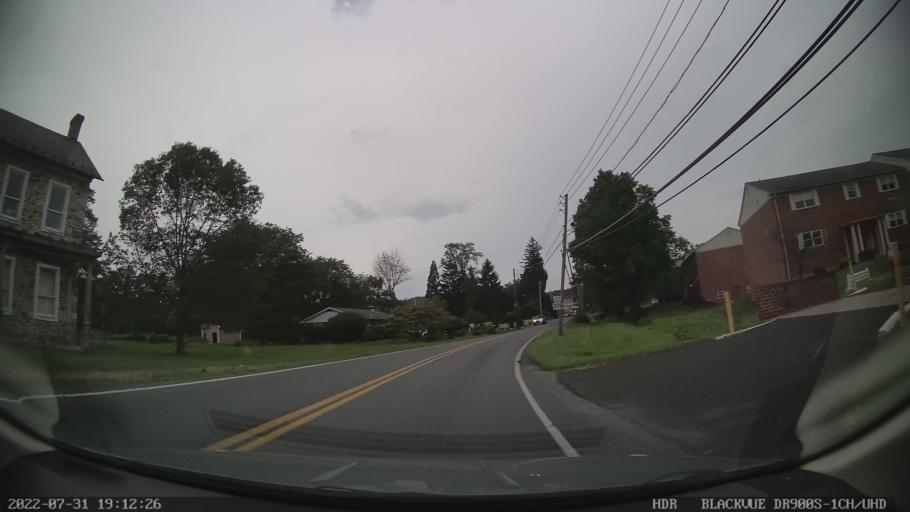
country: US
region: Pennsylvania
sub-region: Lehigh County
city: Fountain Hill
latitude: 40.5792
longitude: -75.3858
